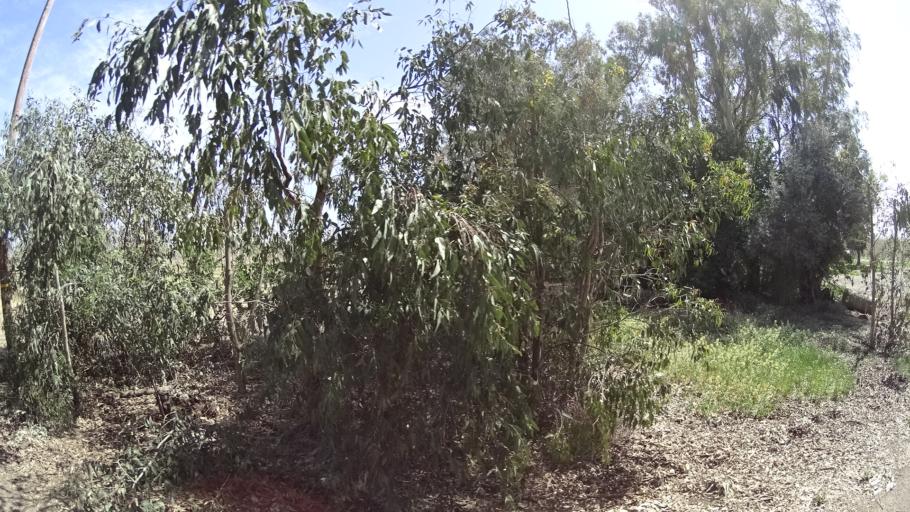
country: US
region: California
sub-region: Glenn County
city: Hamilton City
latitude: 39.6344
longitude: -122.0743
